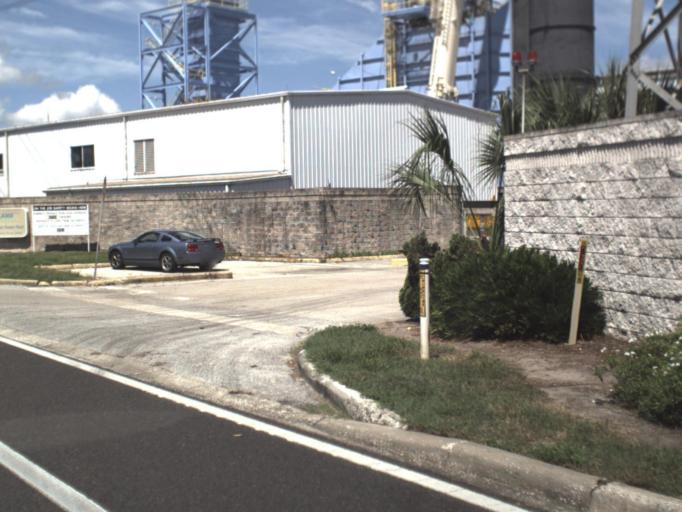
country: US
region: Florida
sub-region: Polk County
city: Crystal Lake
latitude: 28.0485
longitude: -81.9230
